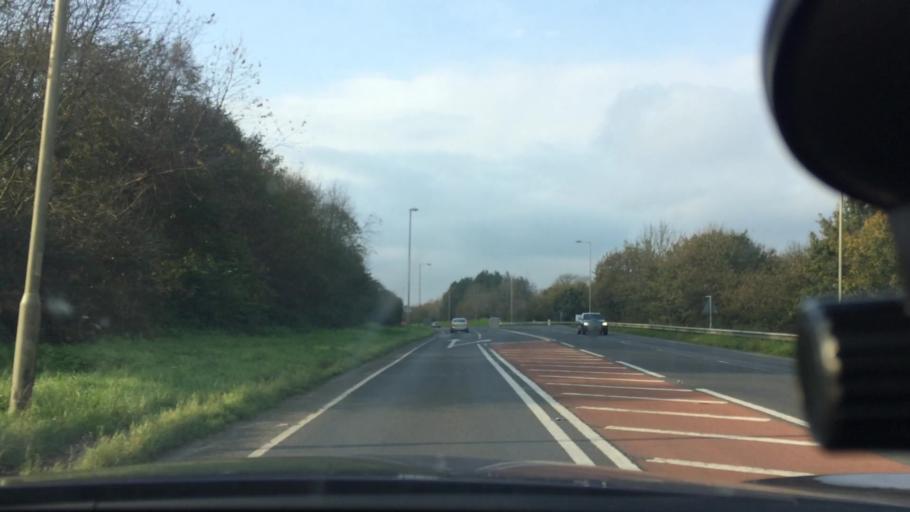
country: GB
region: England
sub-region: Devon
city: Axminster
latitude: 50.7656
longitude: -2.9771
